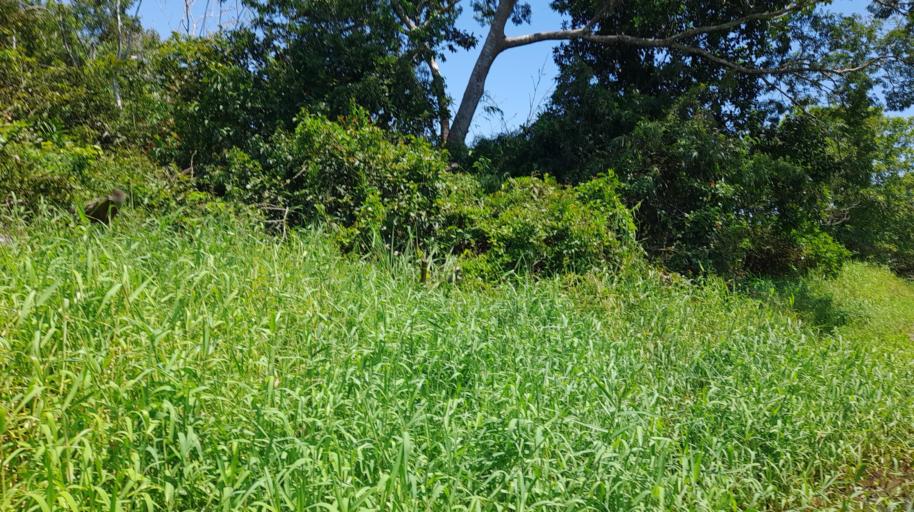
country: PE
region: Ucayali
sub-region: Provincia de Coronel Portillo
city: Puerto Callao
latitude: -8.2666
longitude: -74.6429
